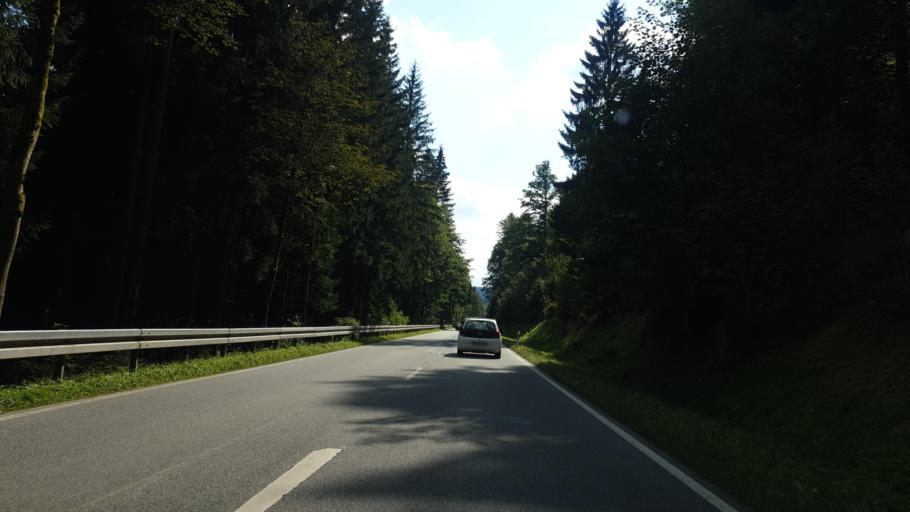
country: DE
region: Saxony
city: Sosa
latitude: 50.4606
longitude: 12.6307
